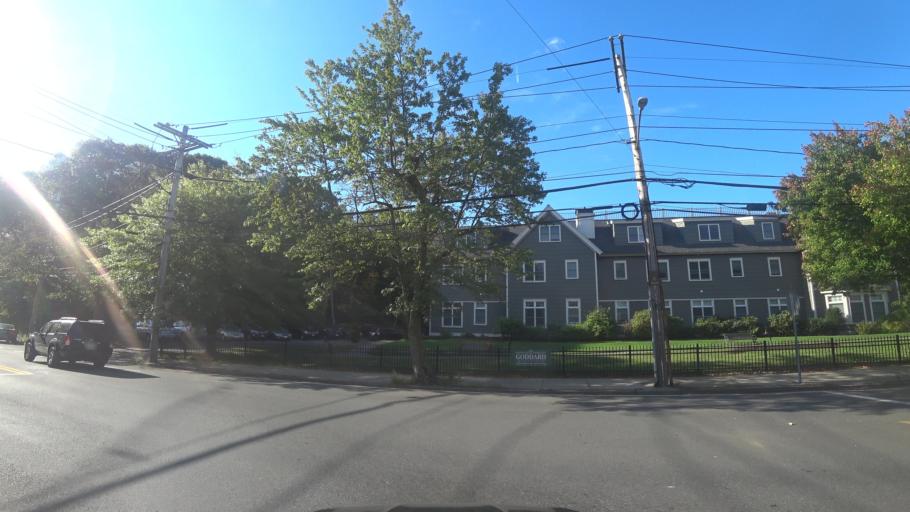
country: US
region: Massachusetts
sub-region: Norfolk County
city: Brookline
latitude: 42.3241
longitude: -71.1217
